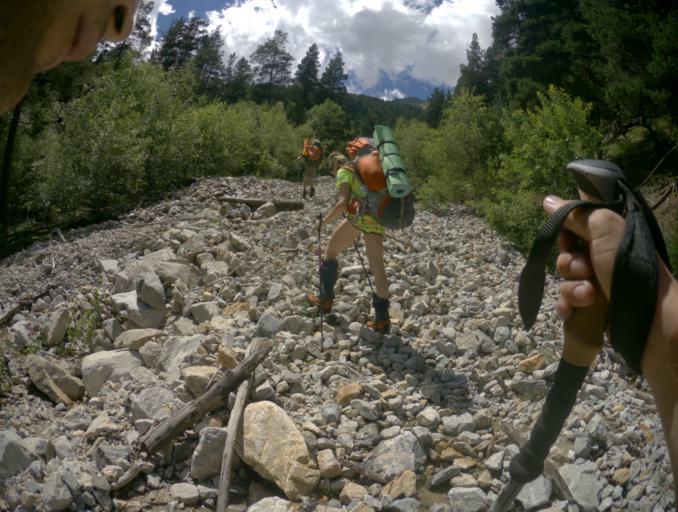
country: RU
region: Karachayevo-Cherkesiya
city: Uchkulan
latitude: 43.3497
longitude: 42.1526
